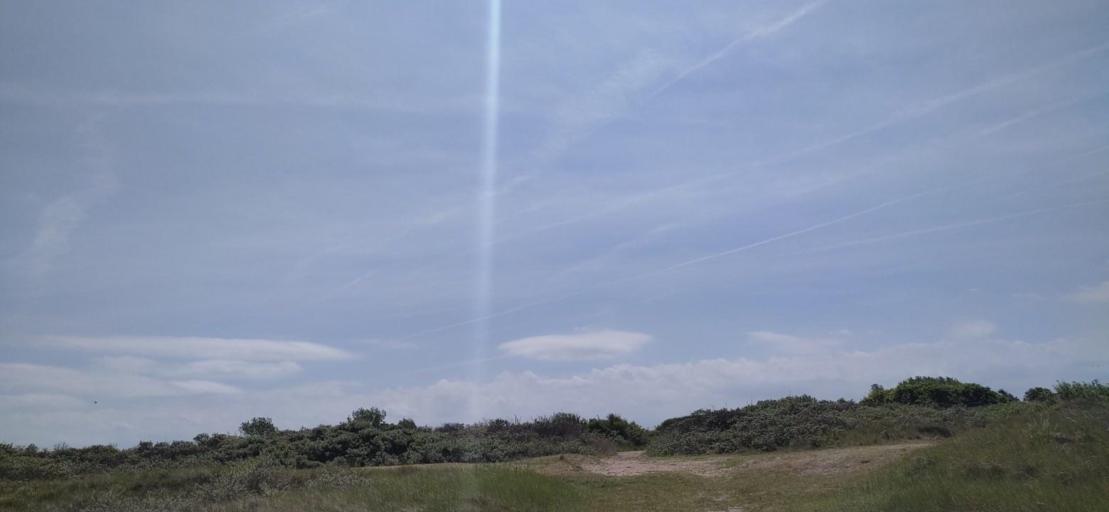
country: FR
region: Nord-Pas-de-Calais
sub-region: Departement du Nord
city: Grand-Fort-Philippe
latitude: 51.0040
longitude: 2.0897
